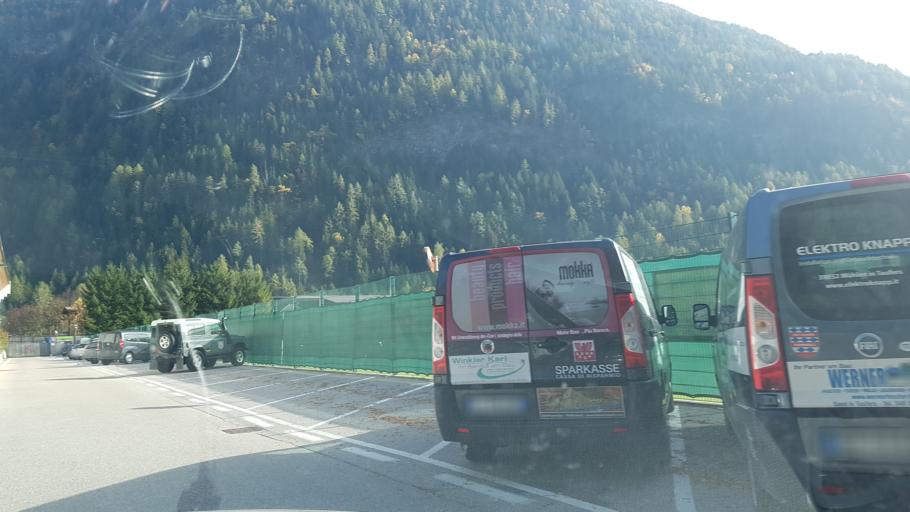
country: IT
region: Trentino-Alto Adige
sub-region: Bolzano
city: Campo Tures
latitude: 46.9112
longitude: 11.9612
